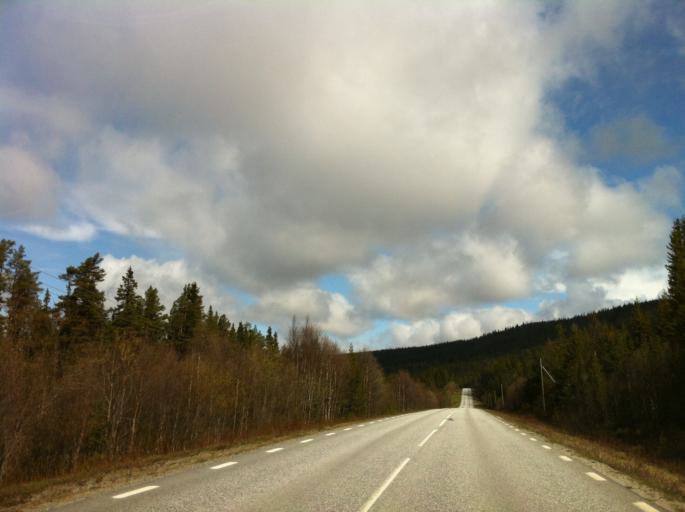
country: SE
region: Jaemtland
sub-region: Are Kommun
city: Are
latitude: 62.5640
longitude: 12.5652
